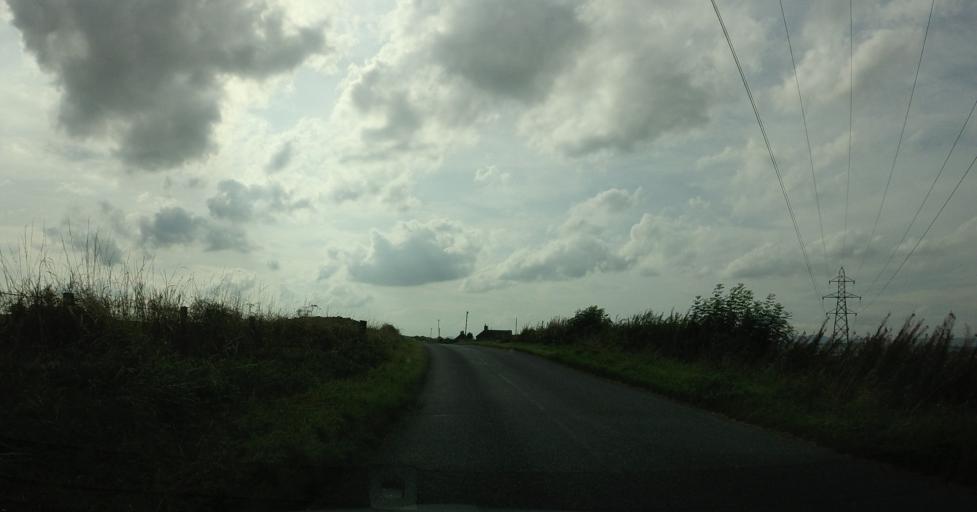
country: GB
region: Scotland
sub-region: Perth and Kinross
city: Methven
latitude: 56.3924
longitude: -3.5726
